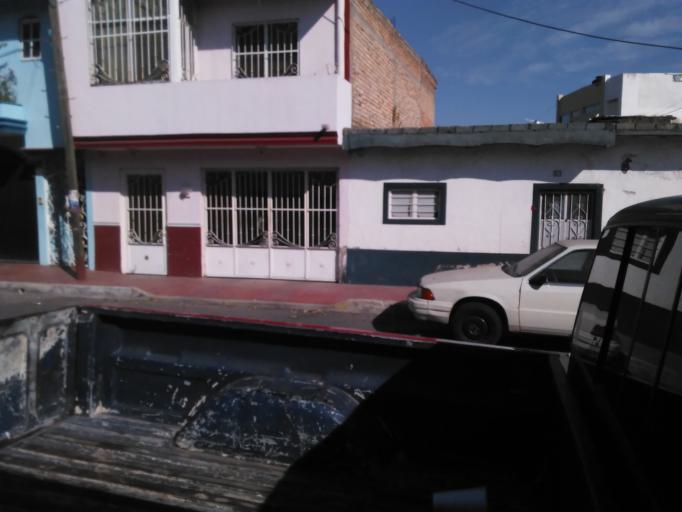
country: MX
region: Nayarit
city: Tepic
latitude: 21.4828
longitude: -104.8917
